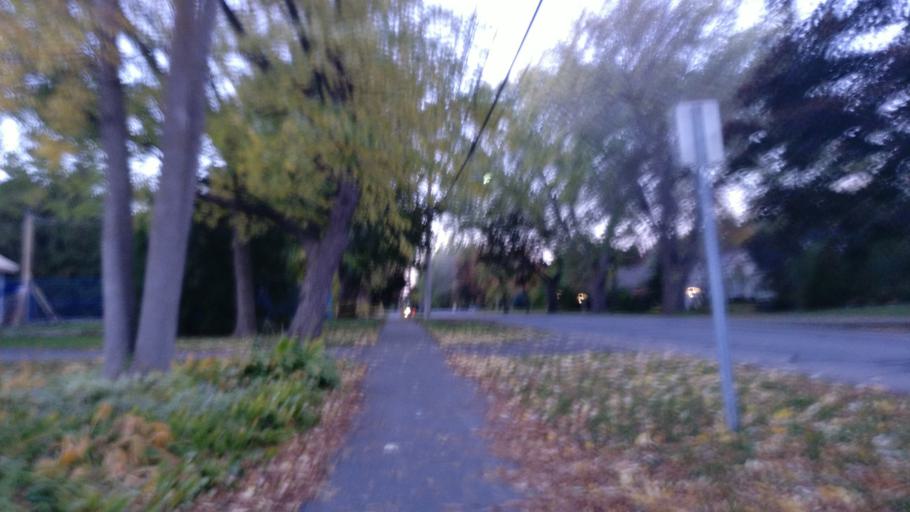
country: CA
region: Quebec
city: Baie-D'Urfe
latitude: 45.4095
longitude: -73.9158
